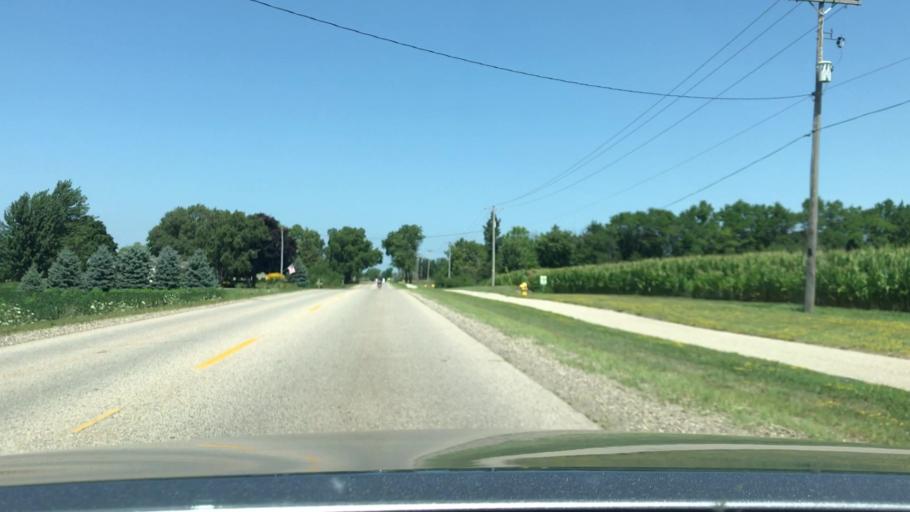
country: US
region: Michigan
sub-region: Ottawa County
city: Holland
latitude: 42.8455
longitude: -86.0790
